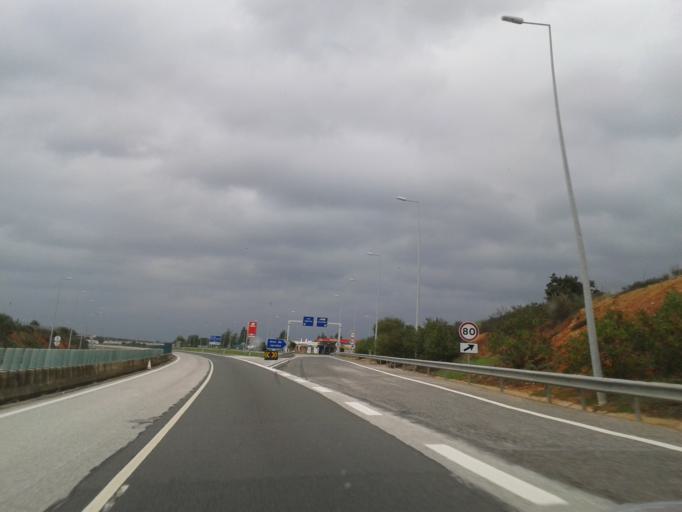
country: PT
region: Faro
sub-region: Lagoa
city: Lagoa
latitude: 37.1499
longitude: -8.4237
